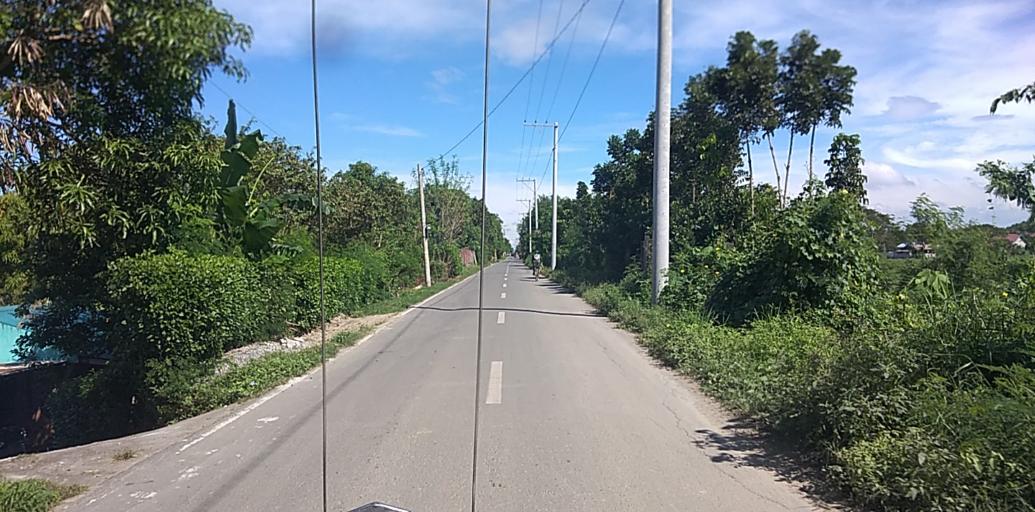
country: PH
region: Central Luzon
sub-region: Province of Pampanga
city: Candaba
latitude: 15.0811
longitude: 120.8090
